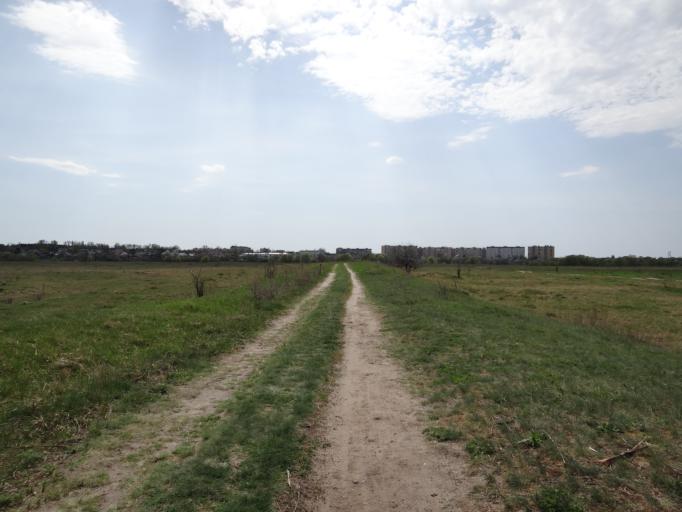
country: RU
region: Kursk
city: Voroshnevo
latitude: 51.6786
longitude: 36.0858
